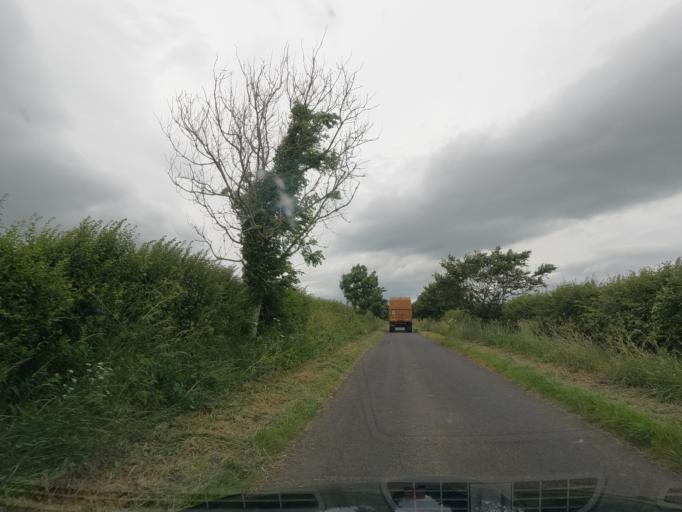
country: GB
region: England
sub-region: Northumberland
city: Lowick
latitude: 55.5734
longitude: -1.9181
